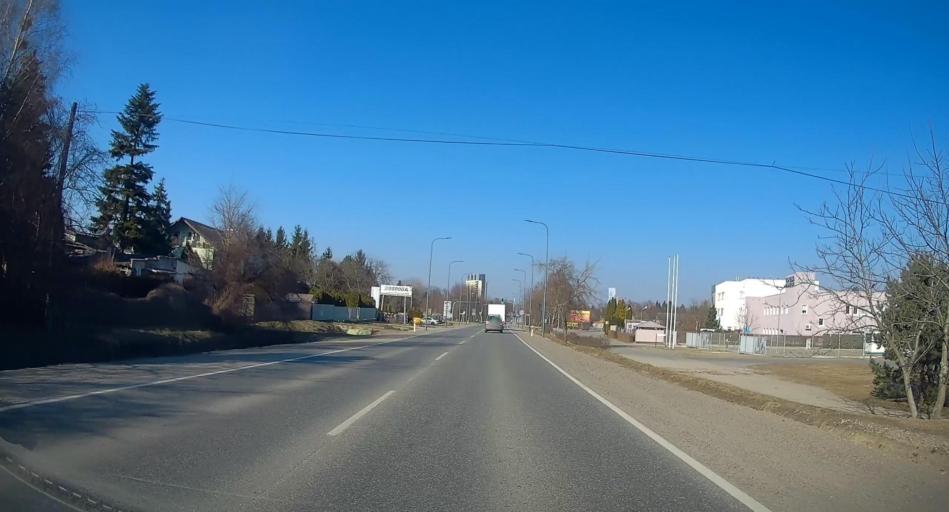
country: PL
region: Masovian Voivodeship
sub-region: Powiat piaseczynski
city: Piaseczno
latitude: 52.0699
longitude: 21.0359
